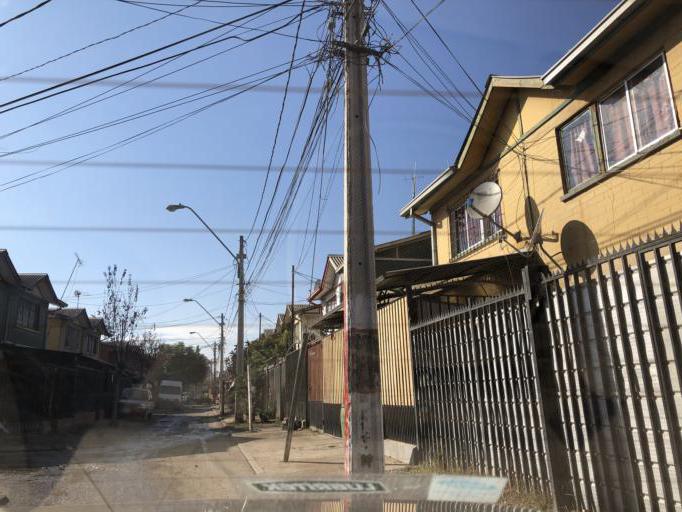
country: CL
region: Santiago Metropolitan
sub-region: Provincia de Cordillera
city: Puente Alto
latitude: -33.6311
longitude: -70.6211
